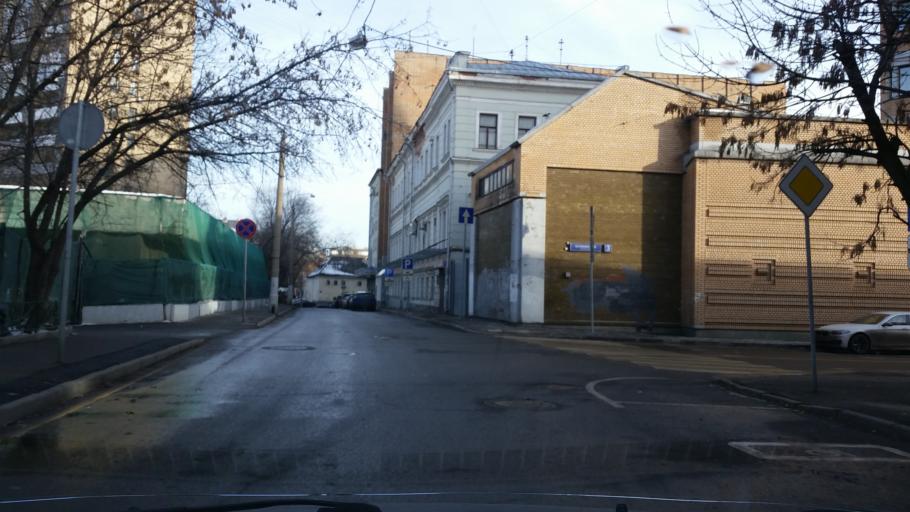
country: RU
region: Moskovskaya
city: Dorogomilovo
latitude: 55.7316
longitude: 37.5871
